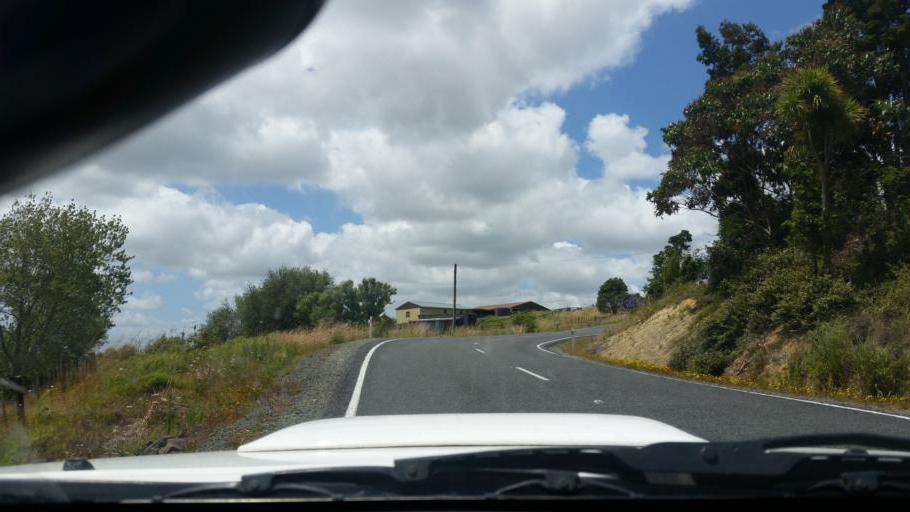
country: NZ
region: Northland
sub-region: Whangarei
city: Ruakaka
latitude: -36.0779
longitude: 174.2435
